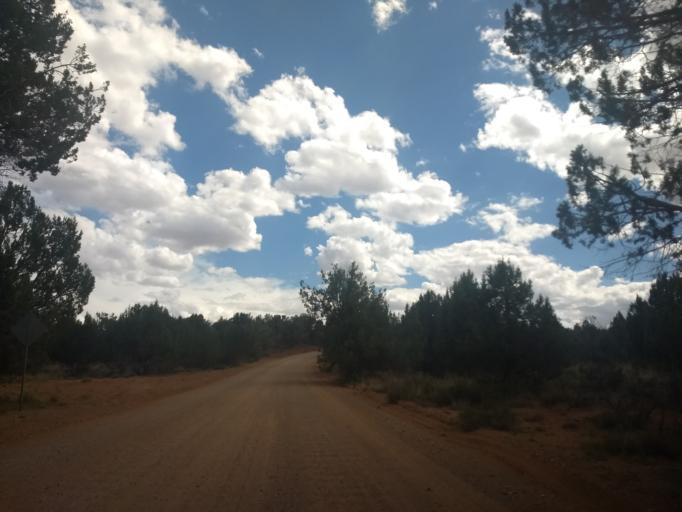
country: US
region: Utah
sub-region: Kane County
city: Kanab
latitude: 37.1501
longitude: -112.5449
